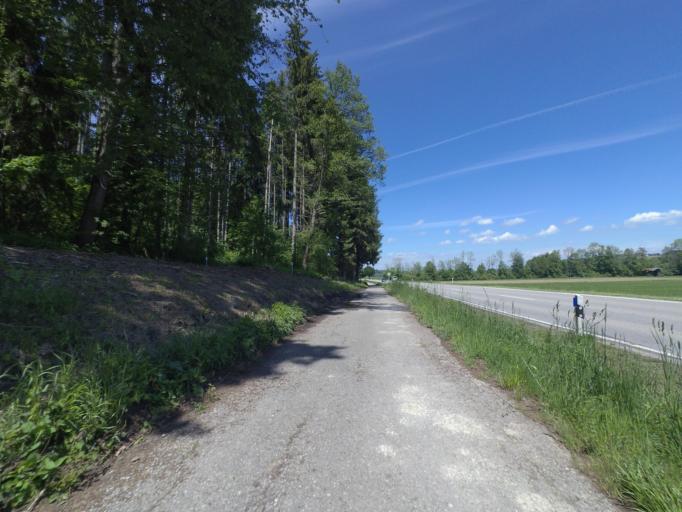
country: DE
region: Bavaria
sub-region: Upper Bavaria
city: Taching am See
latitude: 47.9488
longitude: 12.7351
